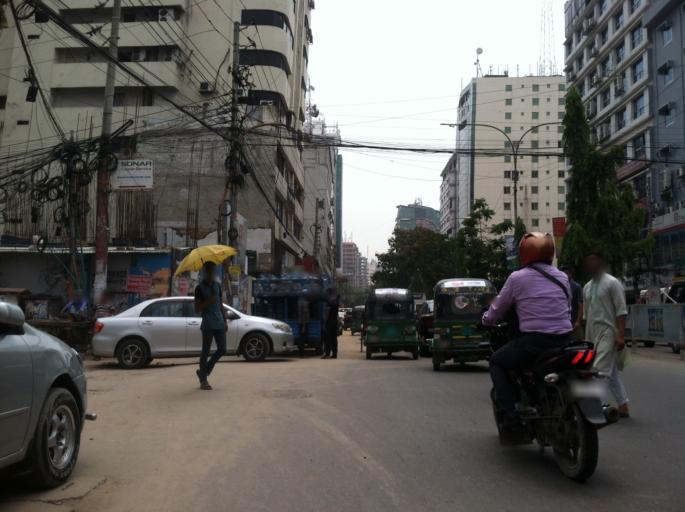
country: BD
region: Dhaka
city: Paltan
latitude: 23.7807
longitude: 90.3985
